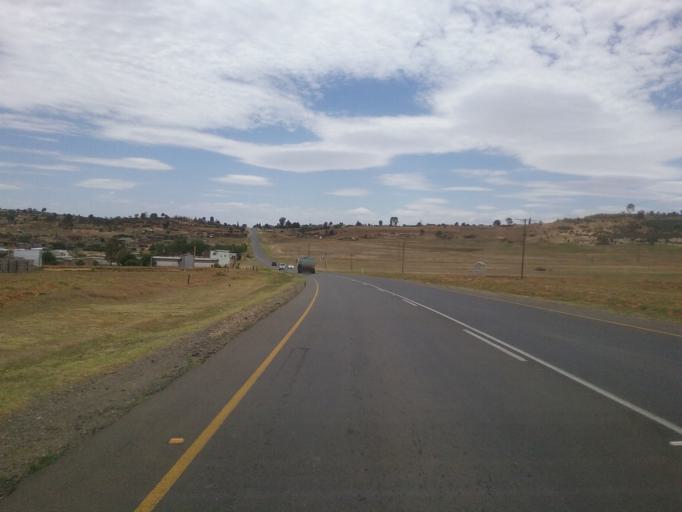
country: LS
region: Maseru
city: Maseru
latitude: -29.5024
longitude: 27.5288
